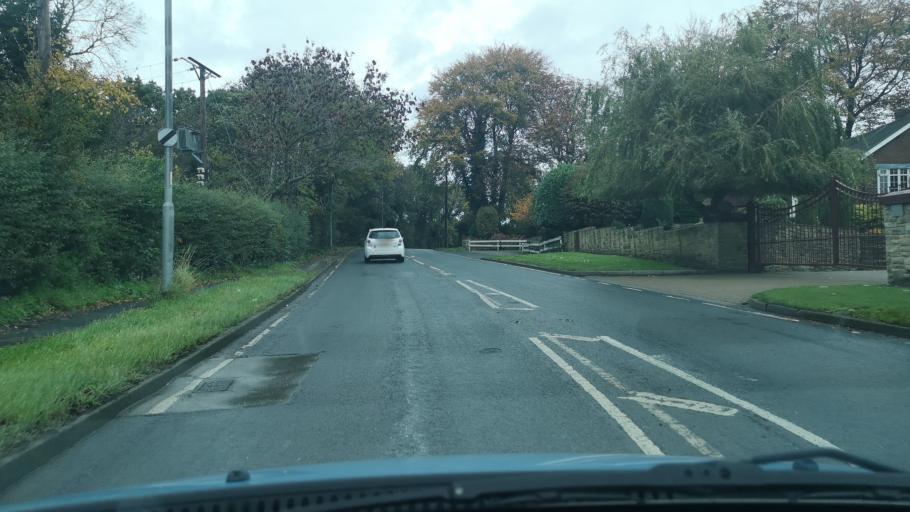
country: GB
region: England
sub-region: City and Borough of Wakefield
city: Hemsworth
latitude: 53.6219
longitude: -1.3438
